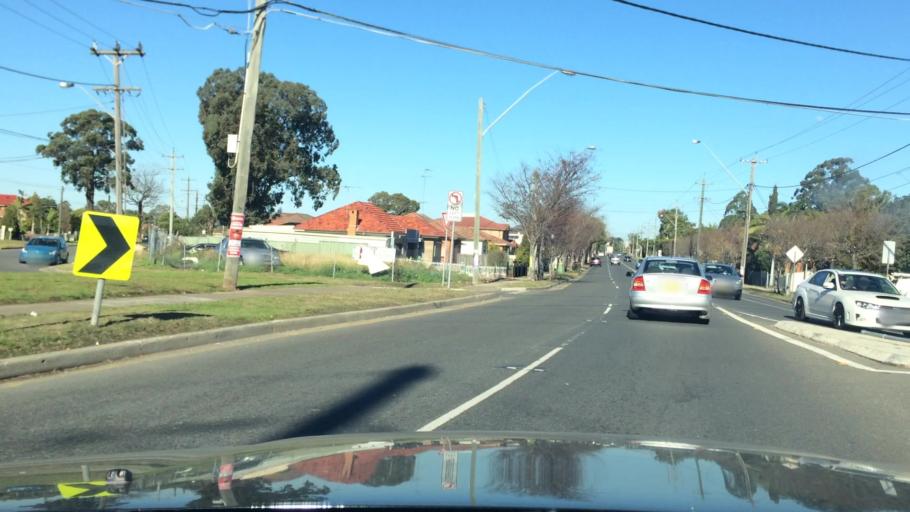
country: AU
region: New South Wales
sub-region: Fairfield
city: Fairfield Heights
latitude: -33.8571
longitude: 150.9507
